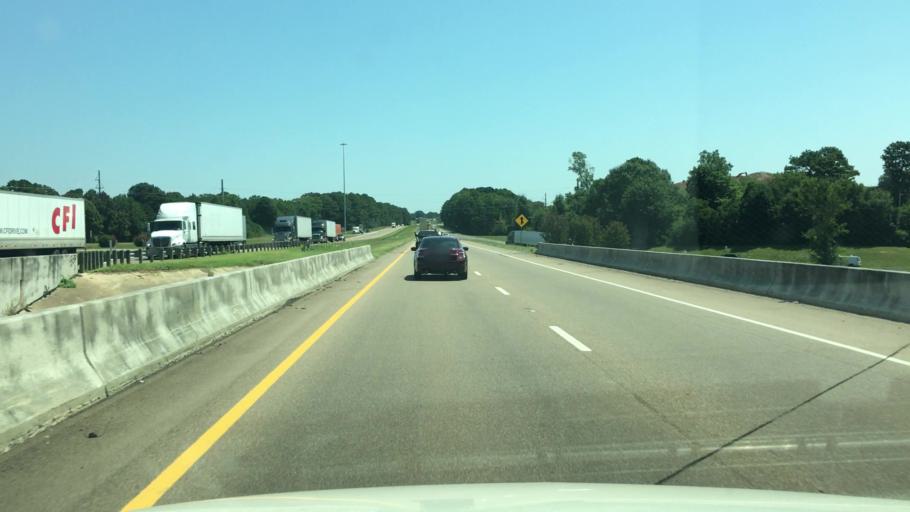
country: US
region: Texas
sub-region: Bowie County
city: New Boston
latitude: 33.4708
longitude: -94.4566
